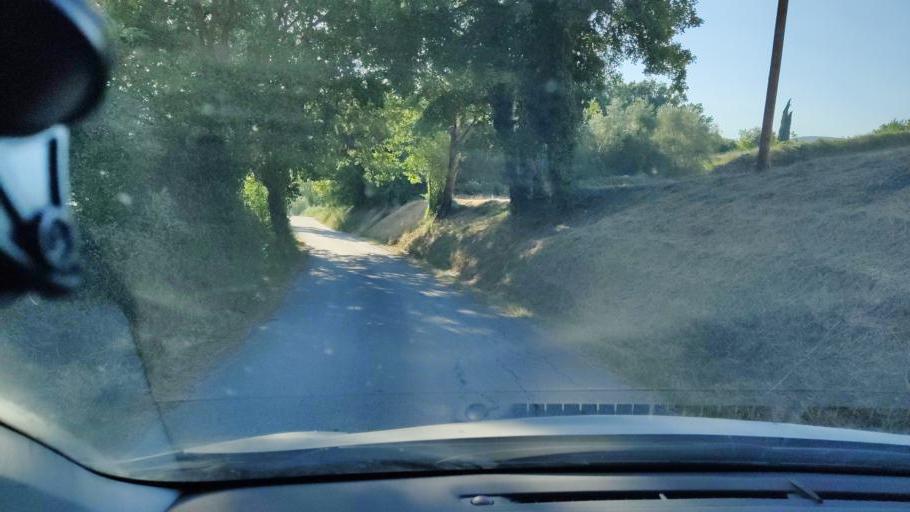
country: IT
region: Umbria
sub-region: Provincia di Terni
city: Amelia
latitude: 42.5444
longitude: 12.3958
